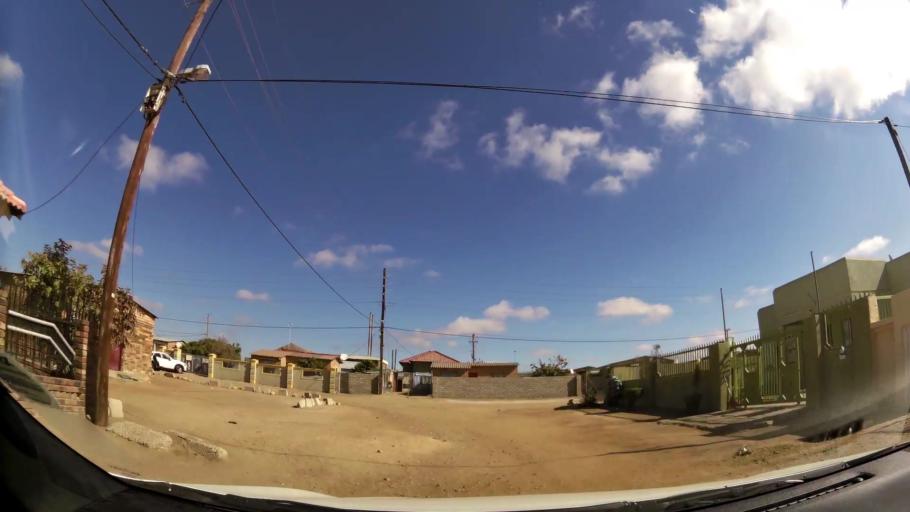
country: ZA
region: Limpopo
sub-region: Capricorn District Municipality
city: Polokwane
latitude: -23.8566
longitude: 29.3975
